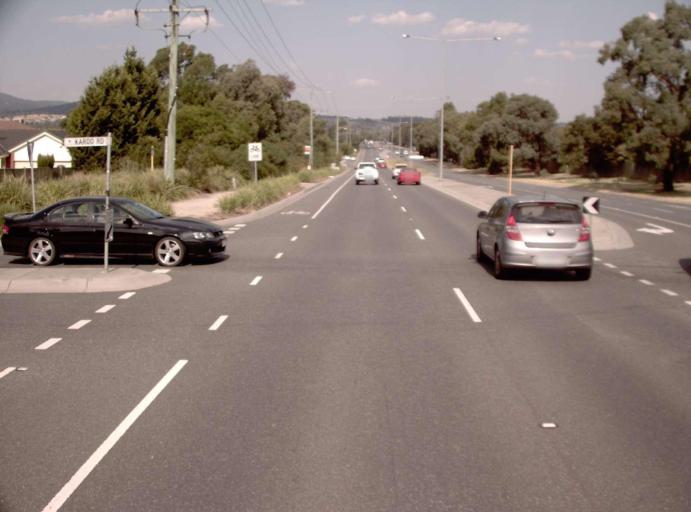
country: AU
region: Victoria
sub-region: Knox
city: Scoresby
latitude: -37.9124
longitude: 145.2522
